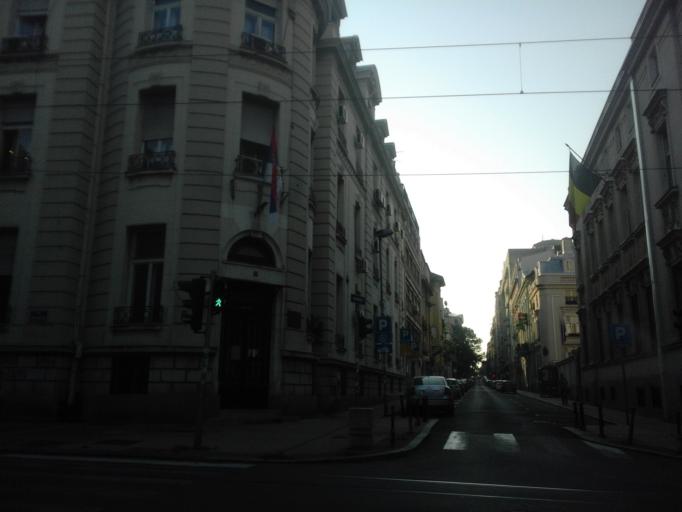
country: RS
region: Central Serbia
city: Belgrade
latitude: 44.8083
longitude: 20.4661
